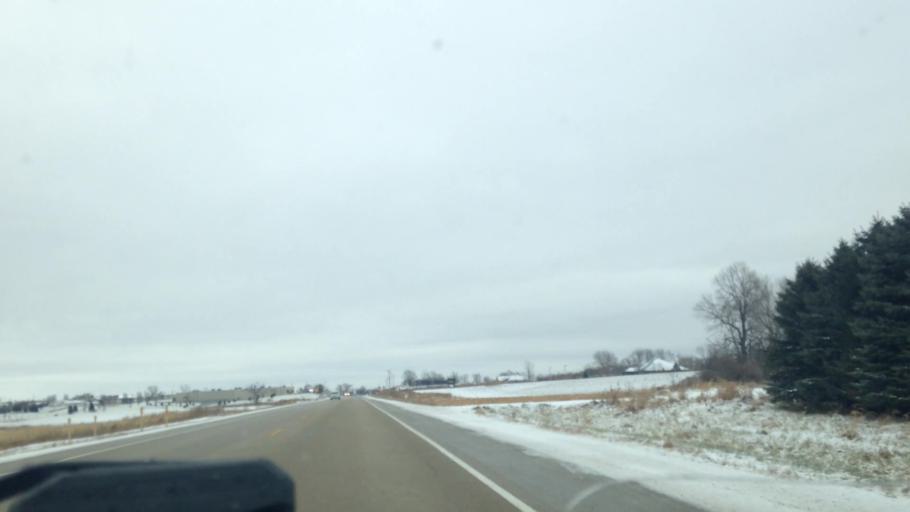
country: US
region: Wisconsin
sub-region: Dodge County
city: Mayville
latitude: 43.4888
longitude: -88.5768
